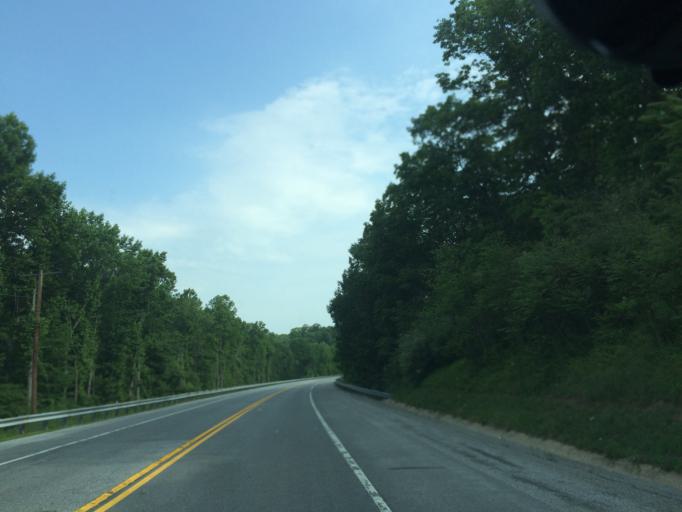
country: US
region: Maryland
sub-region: Carroll County
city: Eldersburg
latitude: 39.4692
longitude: -77.0052
